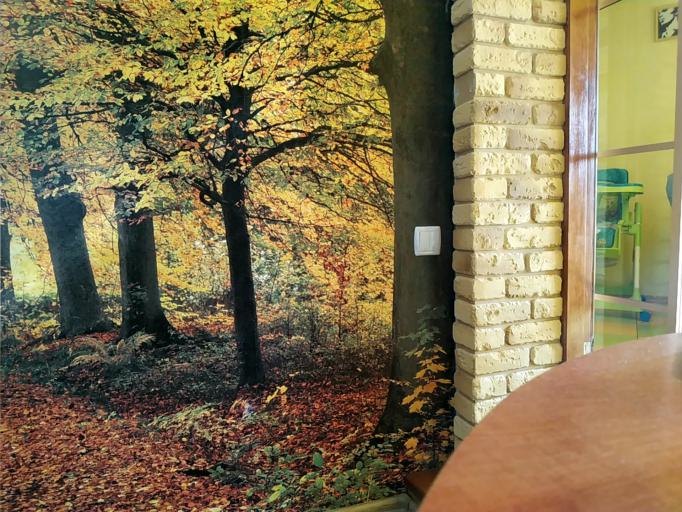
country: RU
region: Novgorod
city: Parfino
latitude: 57.8068
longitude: 31.5872
